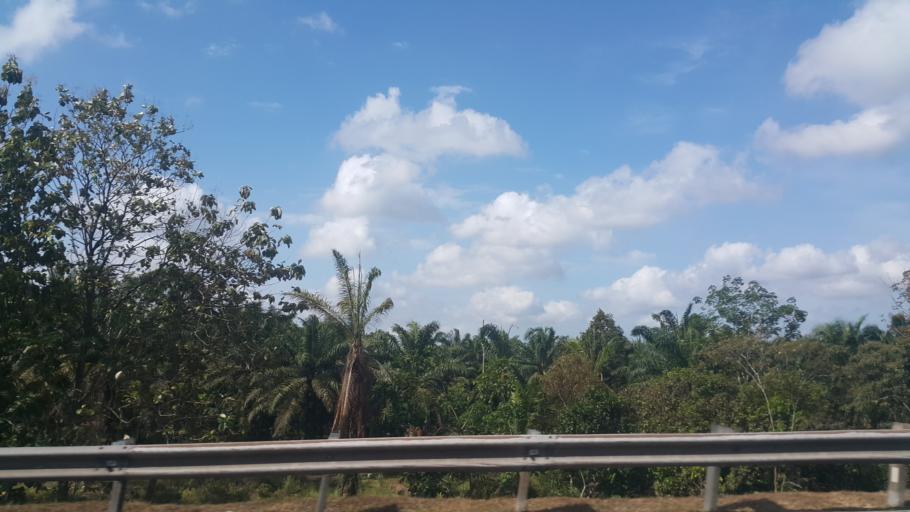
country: MY
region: Johor
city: Parit Raja
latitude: 1.9026
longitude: 103.2163
